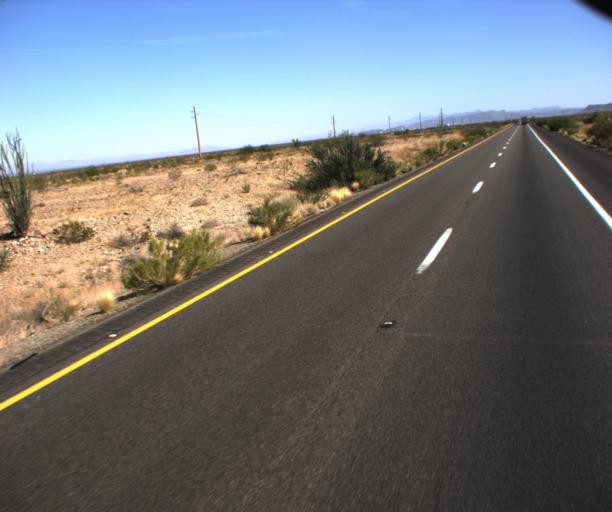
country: US
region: Arizona
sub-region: Mohave County
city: Kingman
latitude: 35.0067
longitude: -114.1351
